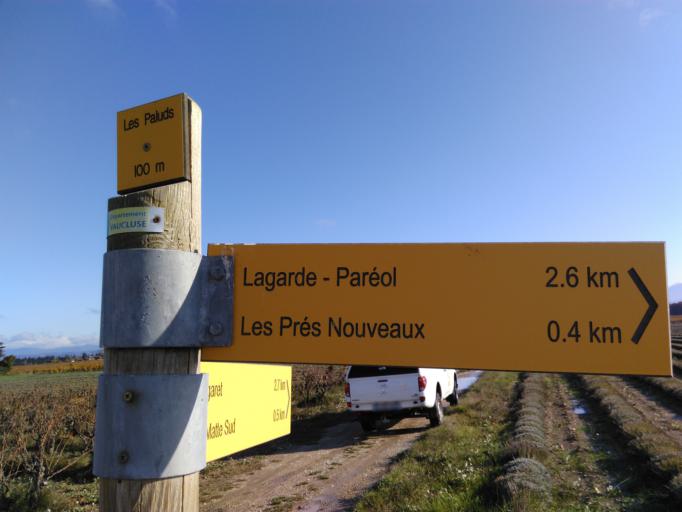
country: FR
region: Provence-Alpes-Cote d'Azur
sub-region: Departement du Vaucluse
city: Sainte-Cecile-les-Vignes
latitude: 44.2382
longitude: 4.8670
